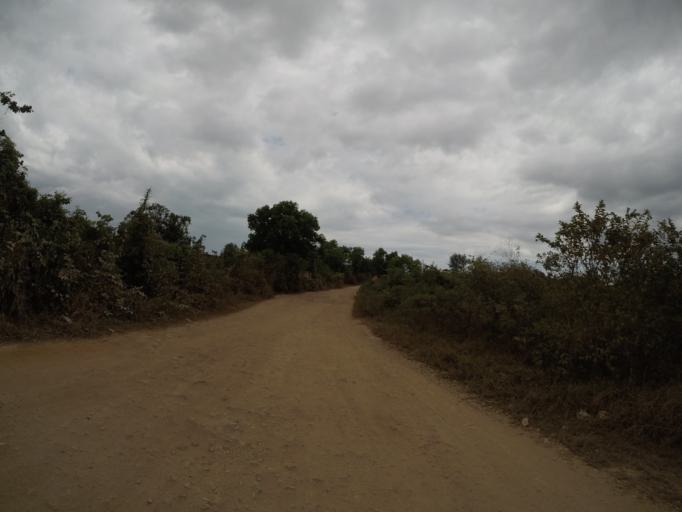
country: TZ
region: Zanzibar Central/South
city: Koani
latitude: -6.1969
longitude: 39.3094
